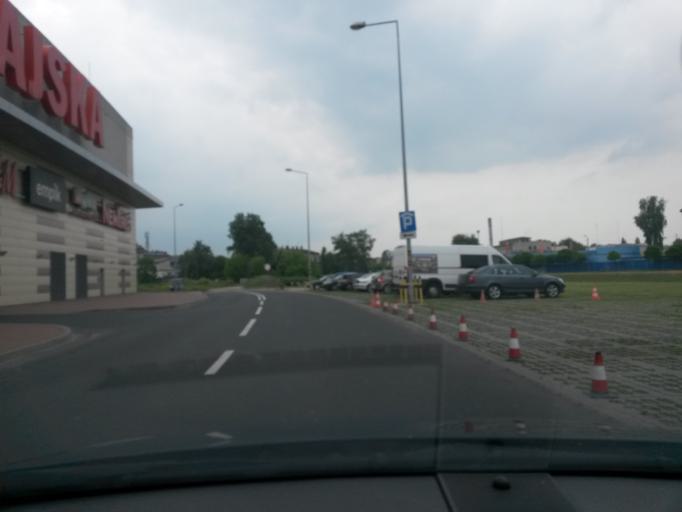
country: PL
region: Silesian Voivodeship
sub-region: Czestochowa
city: Czestochowa
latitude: 50.8081
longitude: 19.1331
